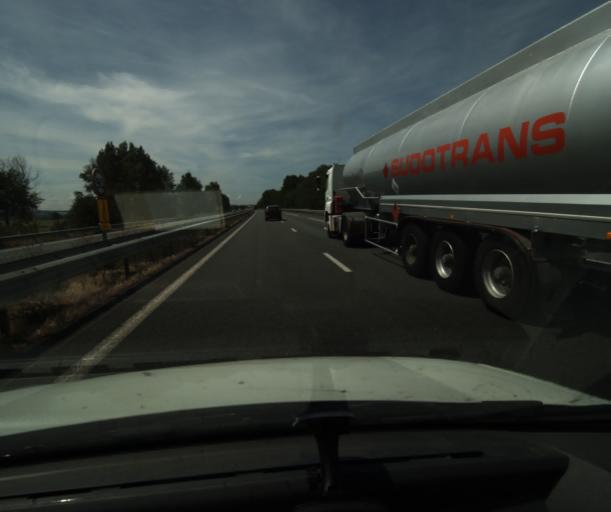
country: FR
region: Languedoc-Roussillon
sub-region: Departement de l'Aude
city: Villepinte
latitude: 43.2459
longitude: 2.0716
